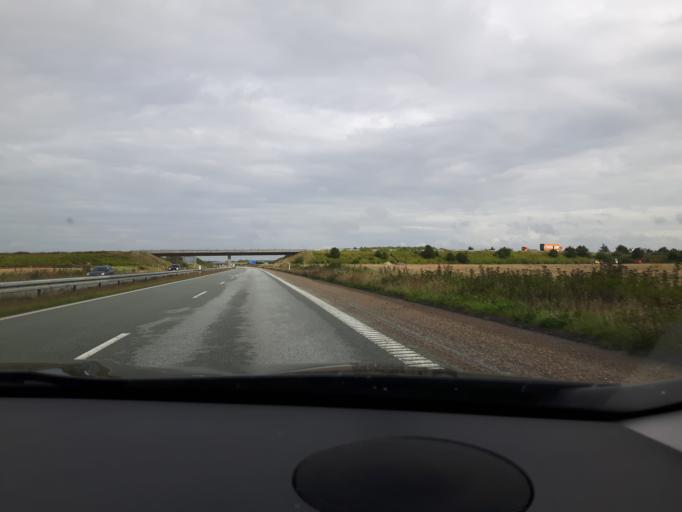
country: DK
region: North Denmark
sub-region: Hjorring Kommune
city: Hjorring
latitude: 57.4453
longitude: 10.0414
